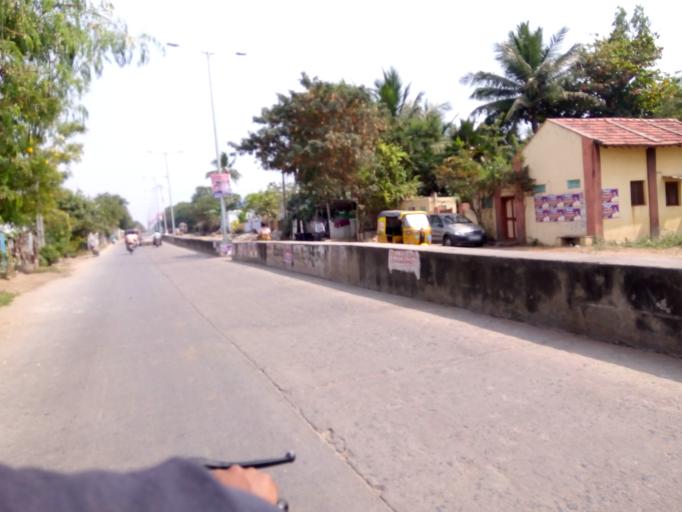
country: IN
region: Andhra Pradesh
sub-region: Prakasam
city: Chirala
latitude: 15.8379
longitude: 80.3668
